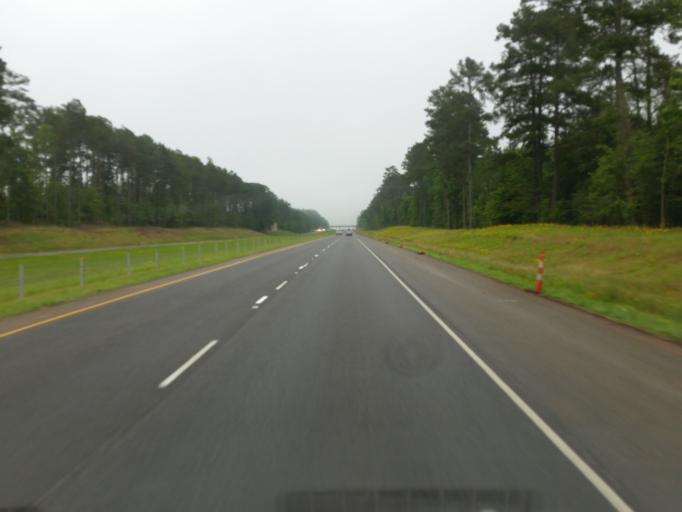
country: US
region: Louisiana
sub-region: Webster Parish
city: Minden
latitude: 32.5617
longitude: -93.1424
